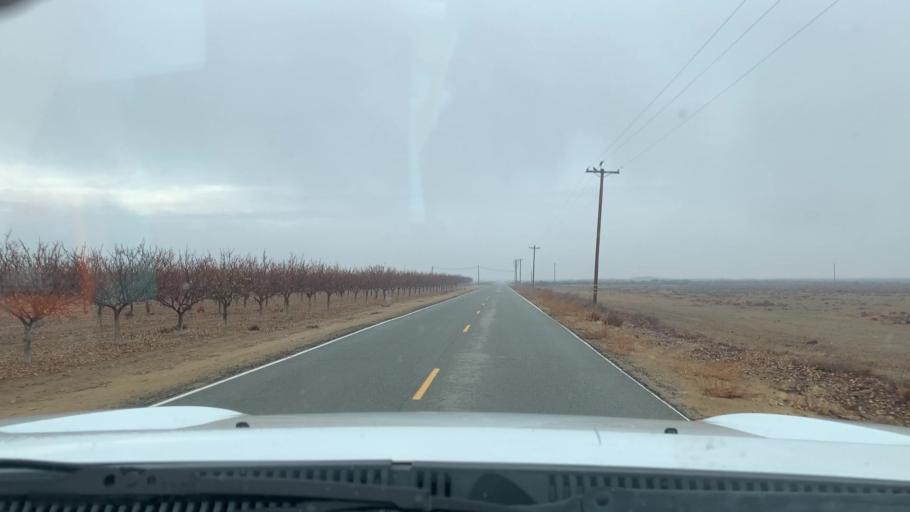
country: US
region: California
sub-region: Kern County
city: Lost Hills
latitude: 35.6339
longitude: -119.5800
